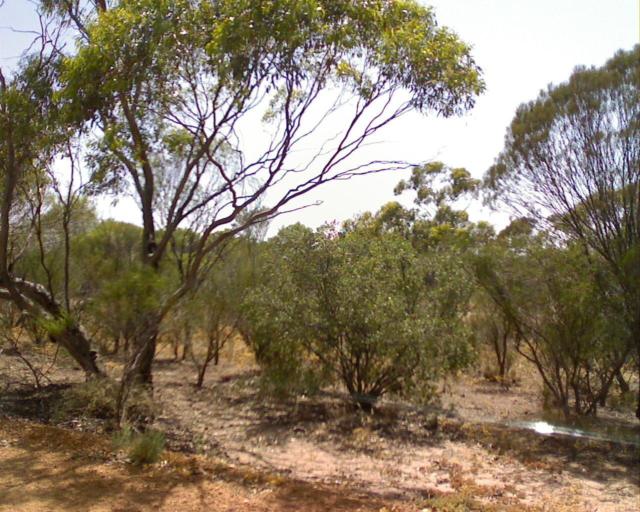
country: AU
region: Western Australia
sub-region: Merredin
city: Merredin
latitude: -30.9958
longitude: 118.3873
